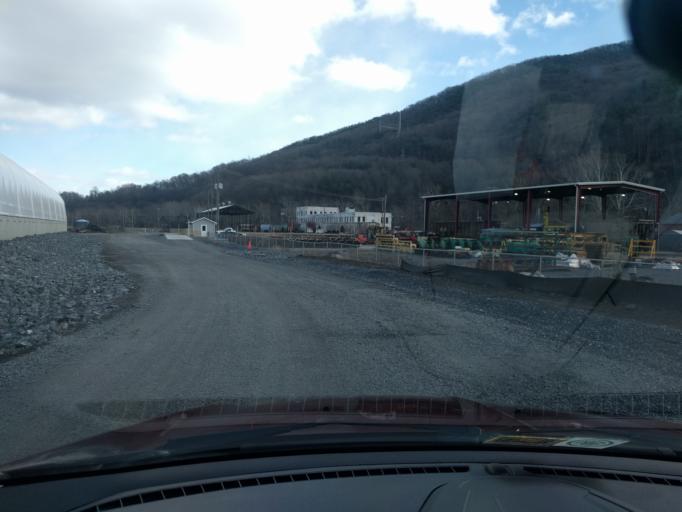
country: US
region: Virginia
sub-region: Alleghany County
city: Clifton Forge
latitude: 37.8090
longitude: -79.8392
